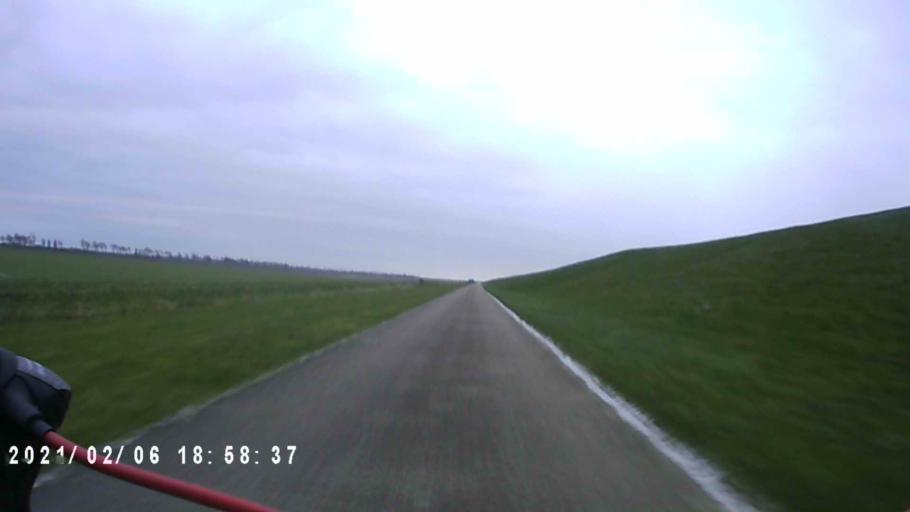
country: NL
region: Groningen
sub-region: Gemeente Winsum
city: Winsum
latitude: 53.4255
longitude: 6.5125
